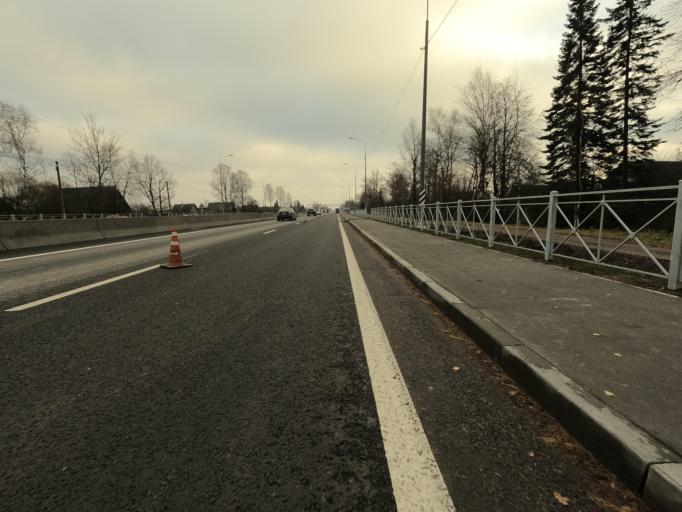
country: RU
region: Leningrad
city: Mga
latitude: 59.7205
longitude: 31.1024
